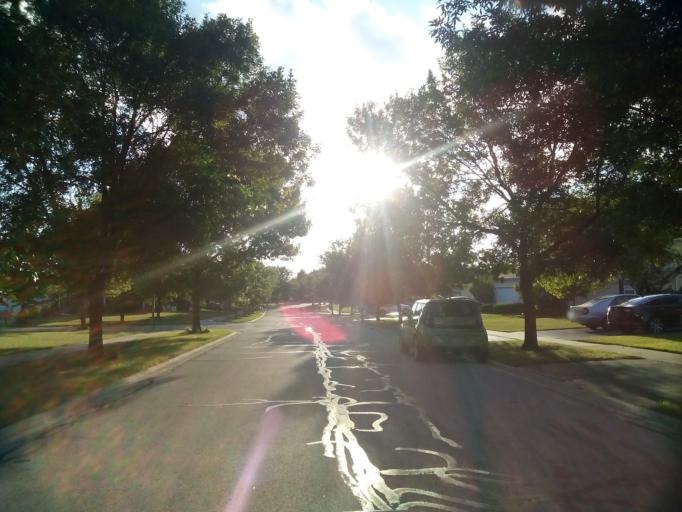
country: US
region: Illinois
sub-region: Will County
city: Romeoville
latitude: 41.6946
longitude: -88.1441
